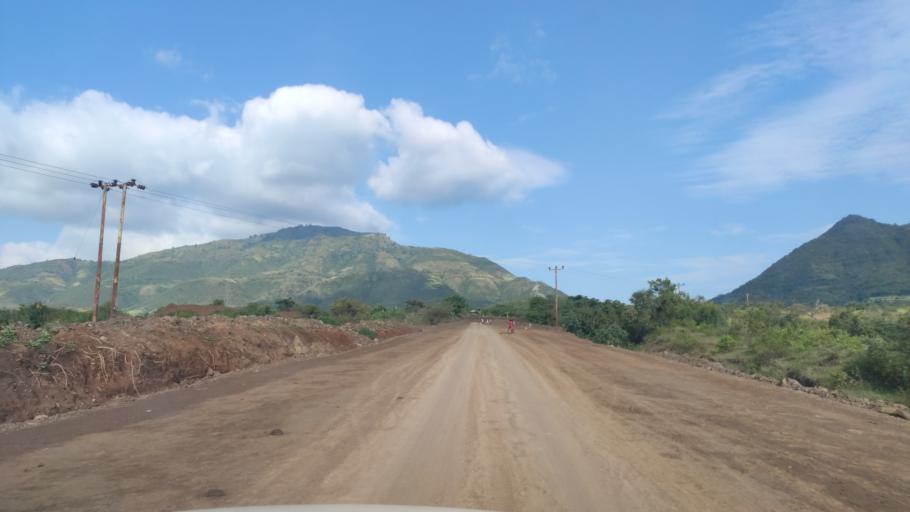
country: ET
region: Southern Nations, Nationalities, and People's Region
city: Arba Minch'
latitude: 6.4269
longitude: 37.3251
